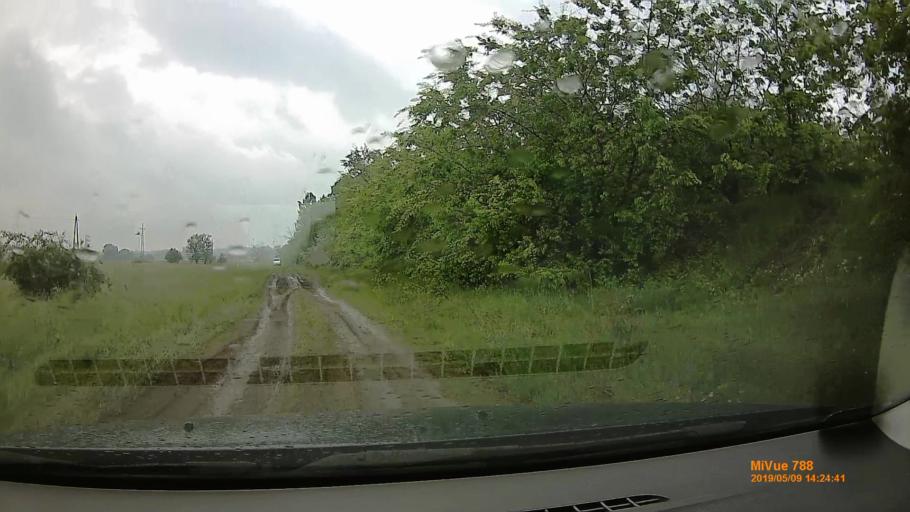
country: HU
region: Budapest
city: Budapest XVII. keruelet
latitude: 47.4992
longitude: 19.2130
